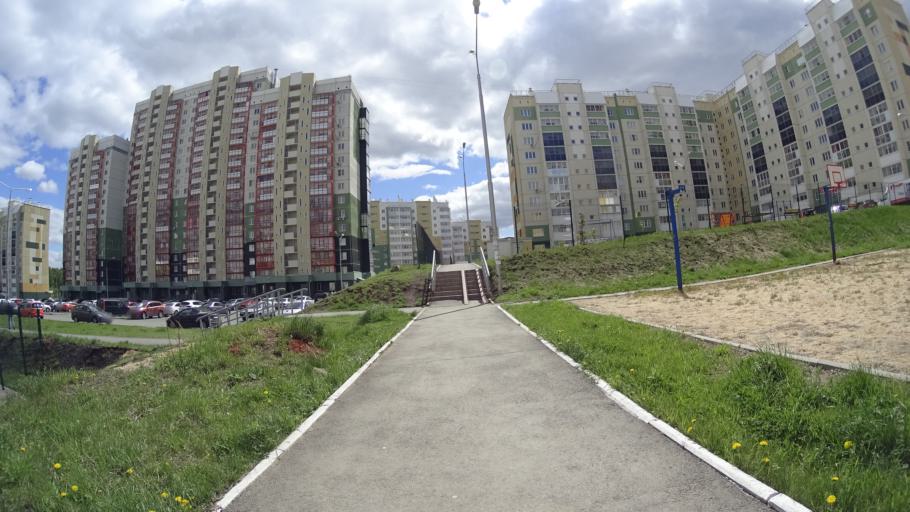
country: RU
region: Chelyabinsk
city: Roshchino
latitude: 55.1732
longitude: 61.2573
